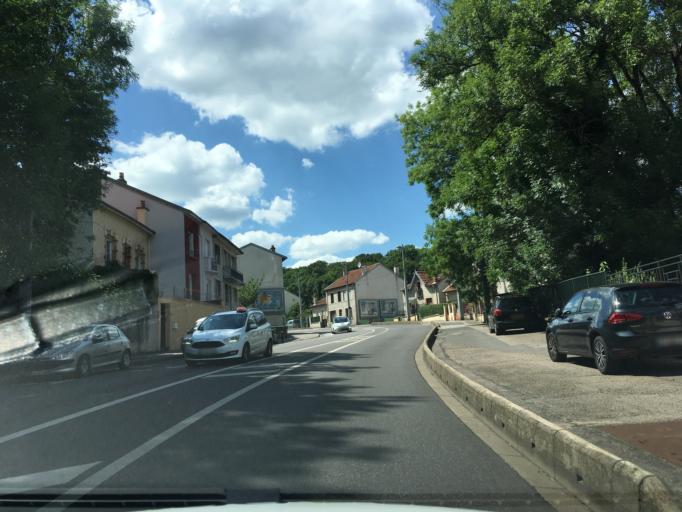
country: FR
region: Lorraine
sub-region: Departement de Meurthe-et-Moselle
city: Laxou
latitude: 48.6965
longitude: 6.1501
